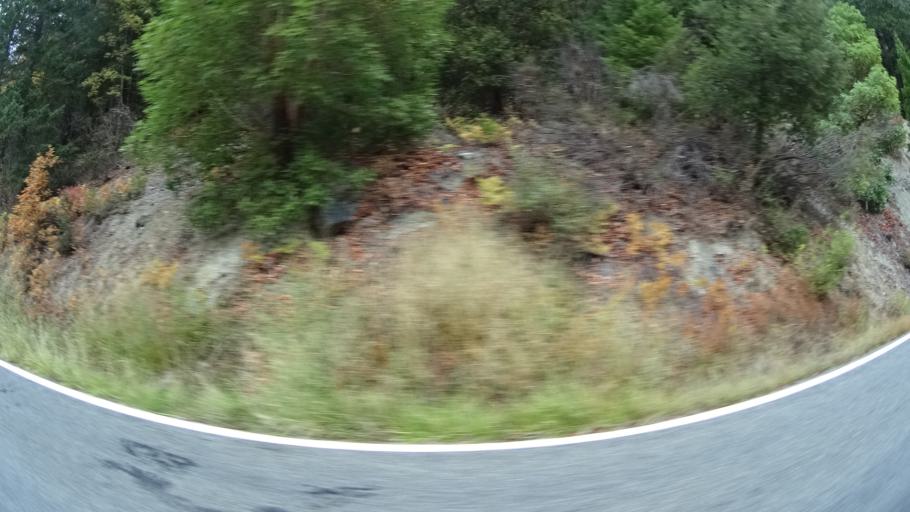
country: US
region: California
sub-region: Siskiyou County
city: Happy Camp
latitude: 41.9103
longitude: -123.4492
